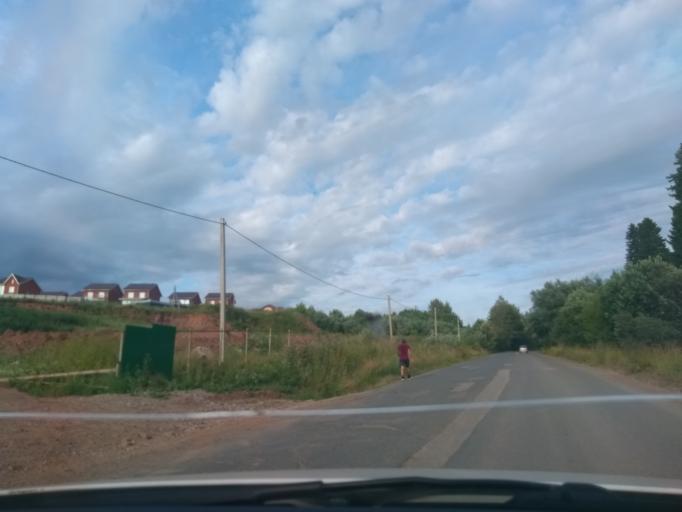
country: RU
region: Perm
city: Perm
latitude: 57.9981
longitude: 56.3231
